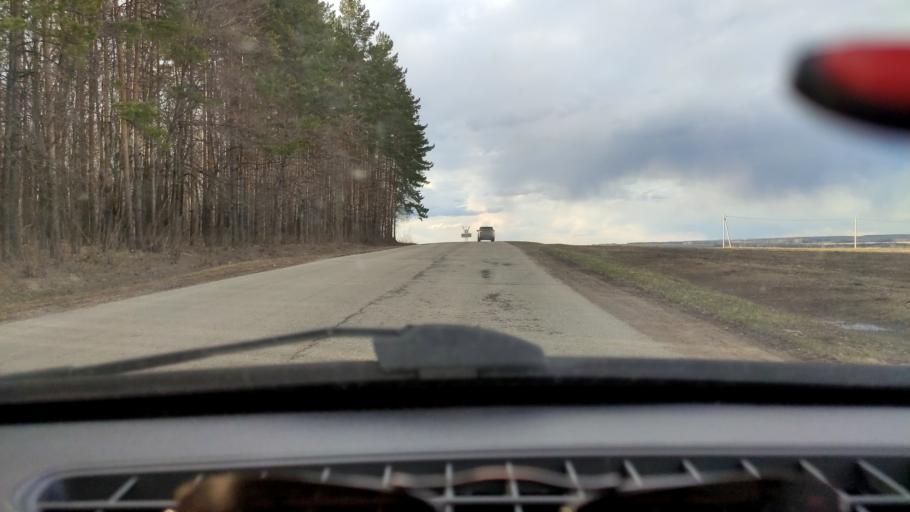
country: RU
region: Bashkortostan
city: Karmaskaly
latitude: 54.3426
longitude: 56.0914
